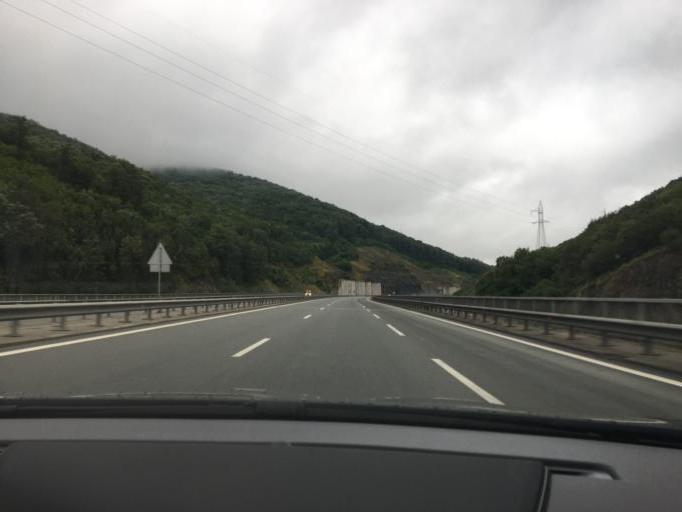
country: BG
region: Sofiya
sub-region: Obshtina Bozhurishte
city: Bozhurishte
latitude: 42.6702
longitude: 23.1502
